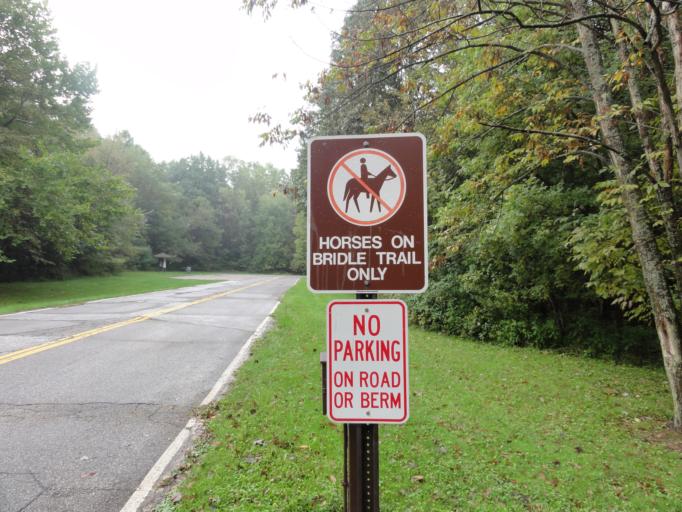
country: US
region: Ohio
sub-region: Cuyahoga County
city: Strongsville
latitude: 41.3112
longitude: -81.7934
